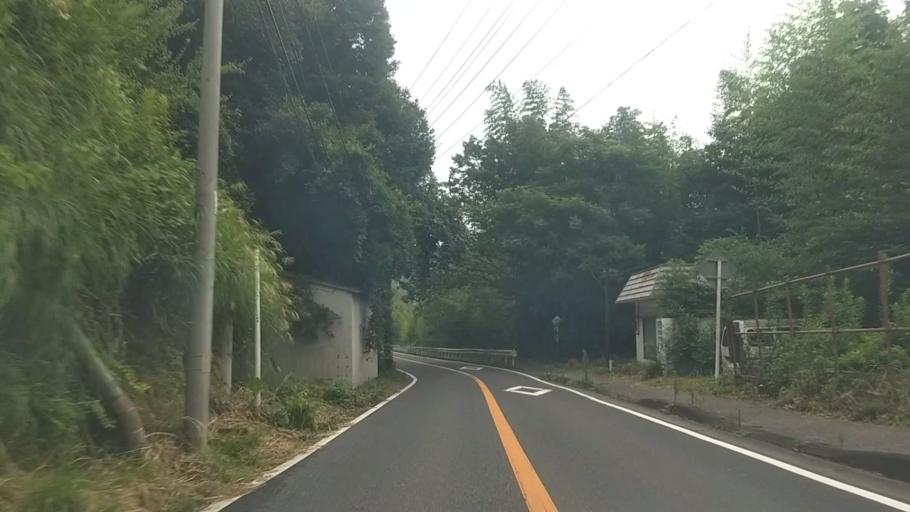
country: JP
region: Chiba
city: Kisarazu
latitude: 35.2930
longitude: 140.0805
